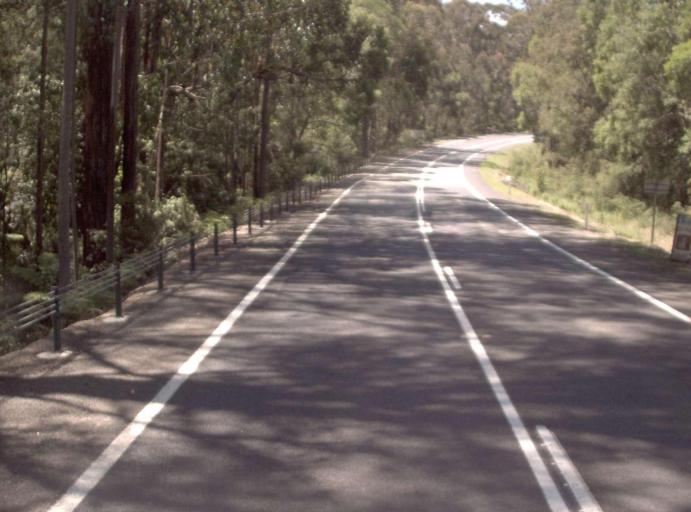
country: AU
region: New South Wales
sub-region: Bombala
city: Bombala
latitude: -37.6518
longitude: 148.8176
